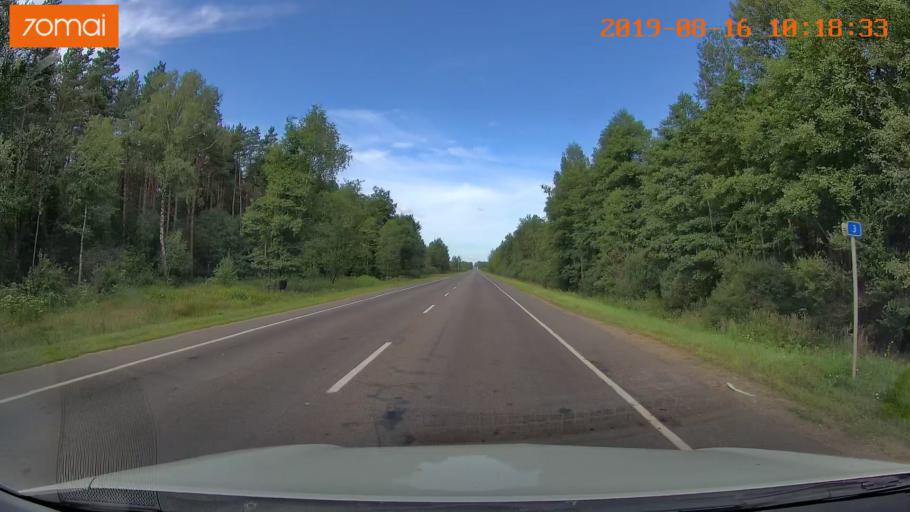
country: BY
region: Mogilev
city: Asipovichy
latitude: 53.3059
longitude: 28.6878
